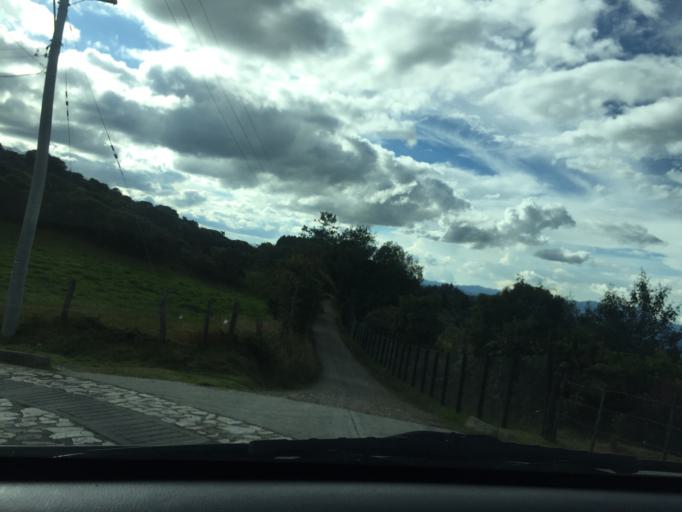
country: CO
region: Cundinamarca
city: Sopo
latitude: 4.9173
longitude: -73.9219
